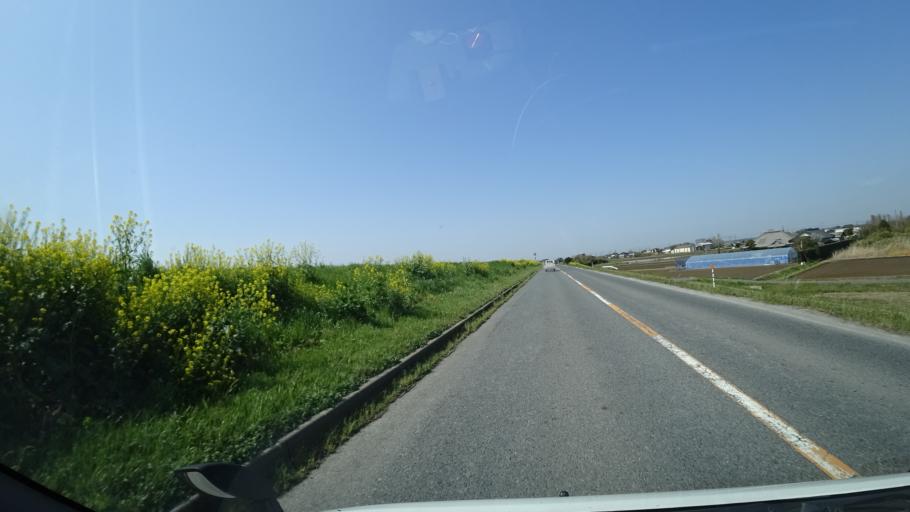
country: JP
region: Chiba
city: Katori-shi
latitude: 35.9183
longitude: 140.4487
